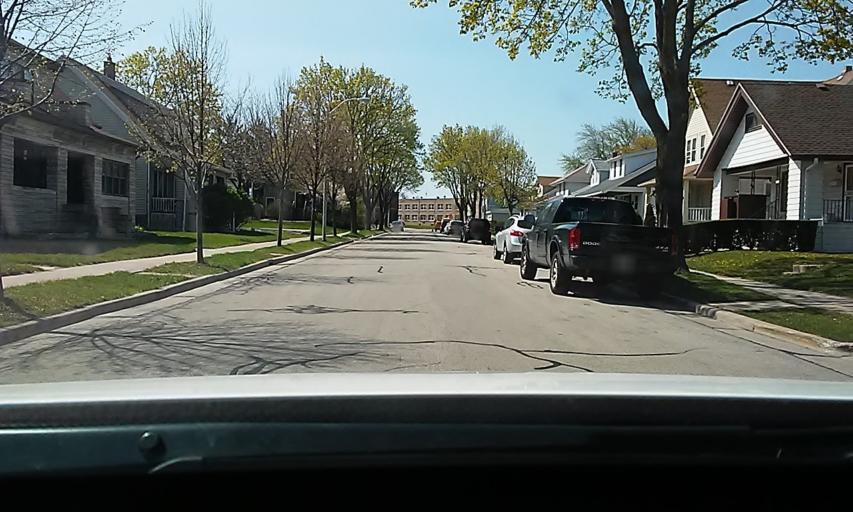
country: US
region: Wisconsin
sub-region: Milwaukee County
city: West Milwaukee
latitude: 43.0188
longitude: -87.9737
